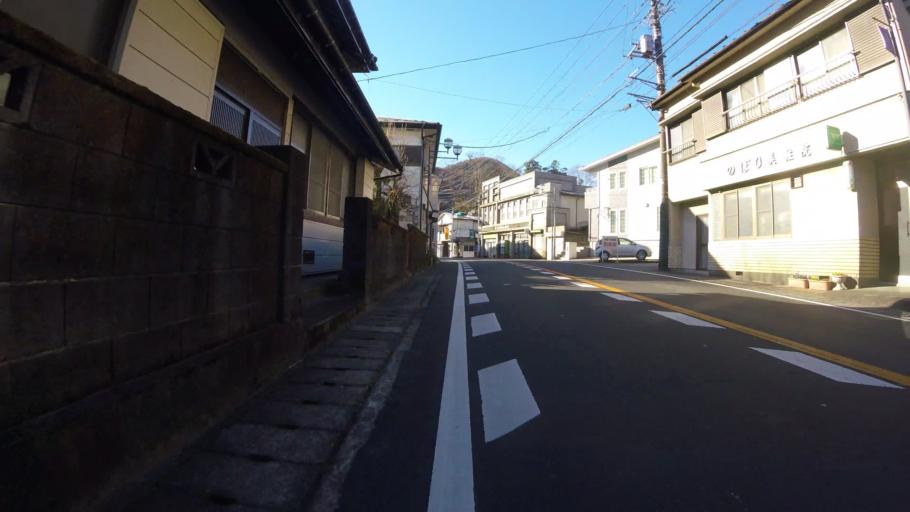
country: JP
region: Shizuoka
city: Heda
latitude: 34.8905
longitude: 138.9290
